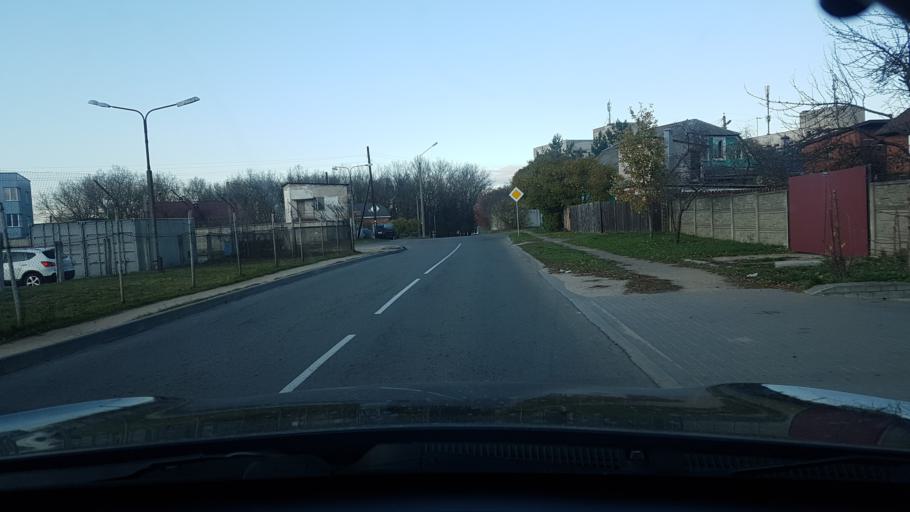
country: BY
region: Minsk
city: Minsk
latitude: 53.9364
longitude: 27.5417
